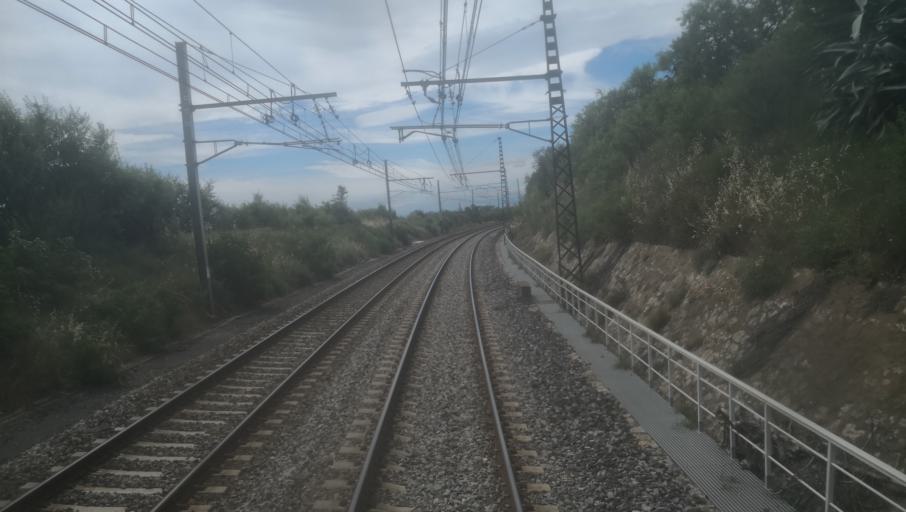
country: FR
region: Languedoc-Roussillon
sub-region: Departement de l'Herault
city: Cers
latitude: 43.3222
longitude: 3.3134
